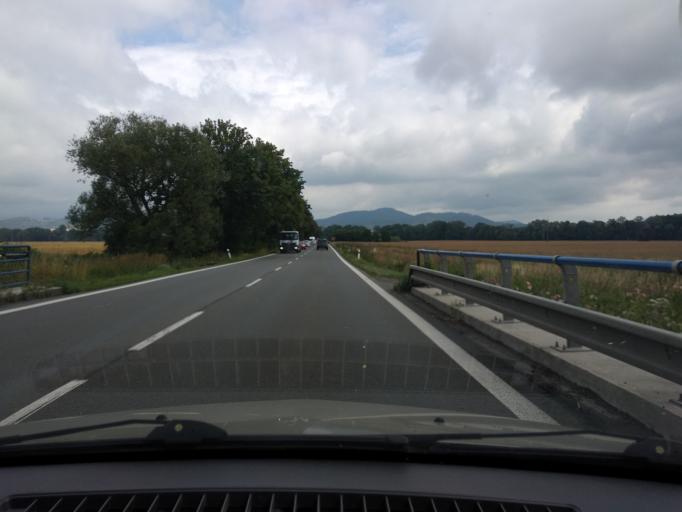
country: CZ
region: Olomoucky
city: Postrelmov
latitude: 49.9197
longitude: 16.9180
